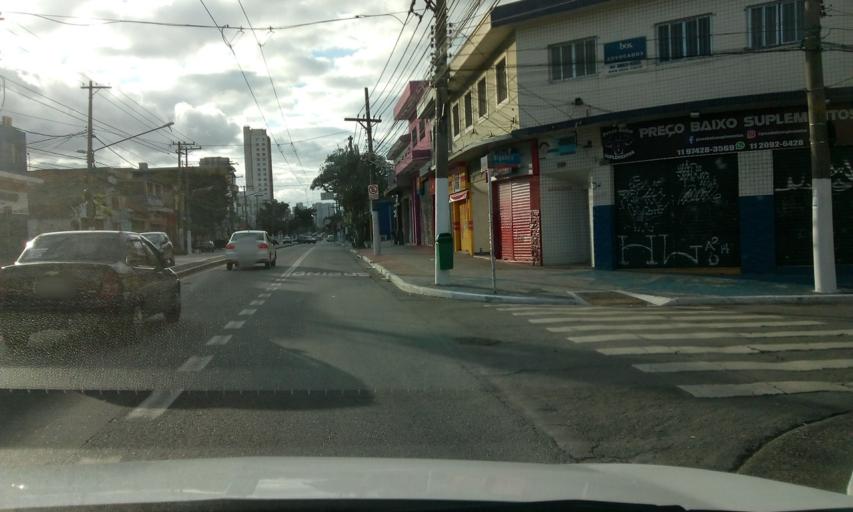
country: BR
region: Sao Paulo
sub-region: Sao Caetano Do Sul
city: Sao Caetano do Sul
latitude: -23.5519
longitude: -46.5300
